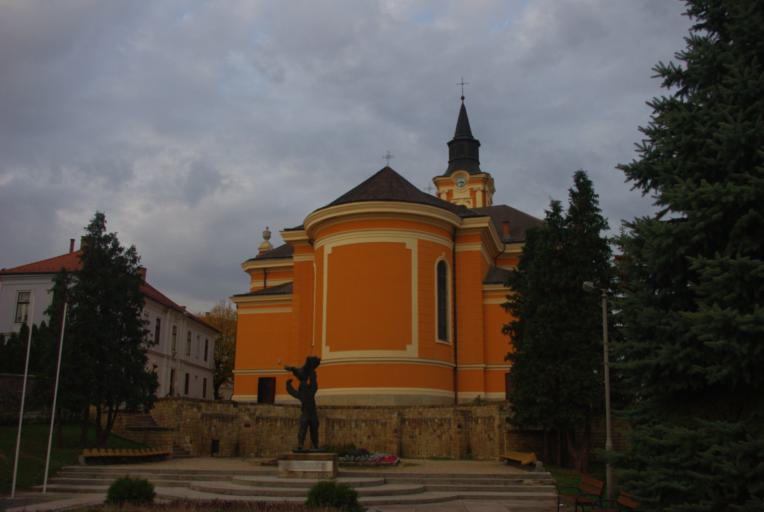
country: HU
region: Borsod-Abauj-Zemplen
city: Satoraljaujhely
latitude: 48.3941
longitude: 21.6558
